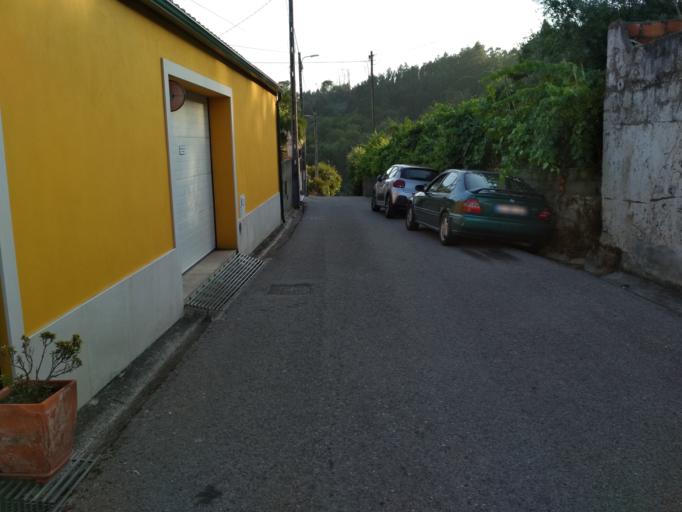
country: PT
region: Coimbra
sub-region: Coimbra
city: Coimbra
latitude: 40.2666
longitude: -8.4524
